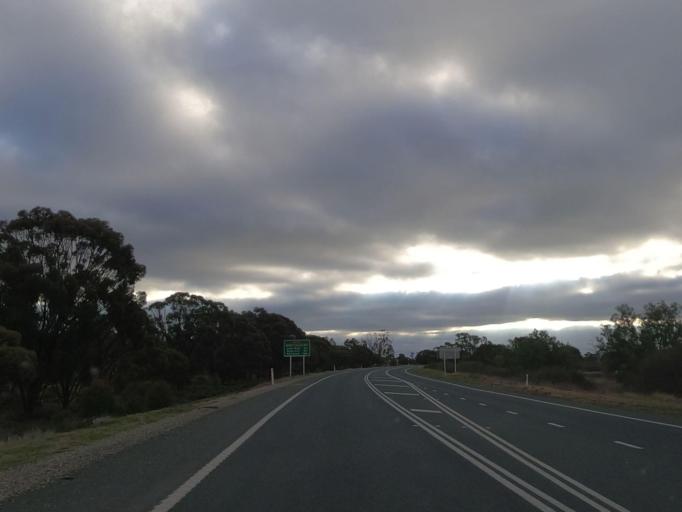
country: AU
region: Victoria
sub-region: Swan Hill
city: Swan Hill
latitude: -35.7335
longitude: 143.8987
